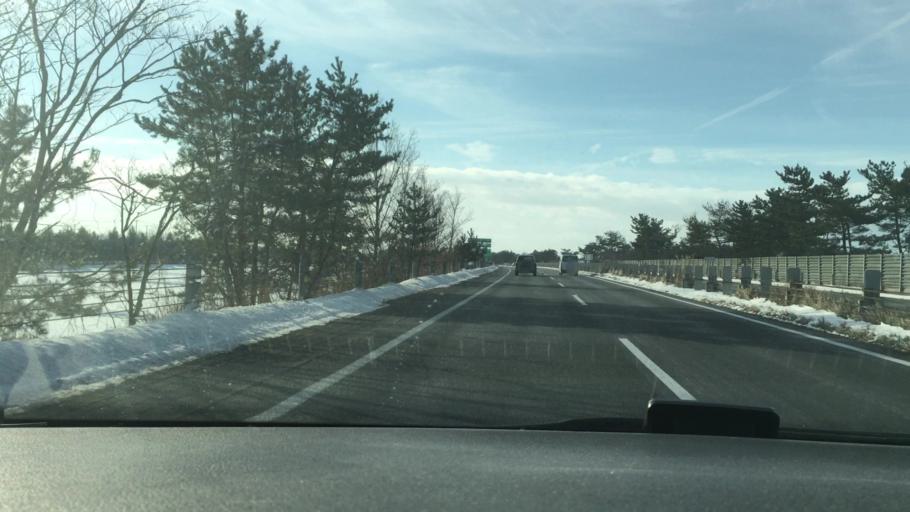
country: JP
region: Iwate
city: Hanamaki
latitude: 39.3615
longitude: 141.0902
